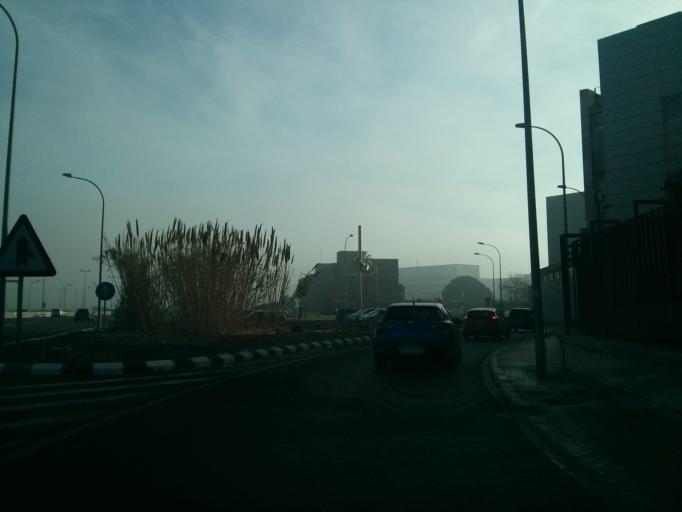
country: ES
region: Valencia
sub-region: Provincia de Valencia
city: Alboraya
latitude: 39.4830
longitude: -0.3485
